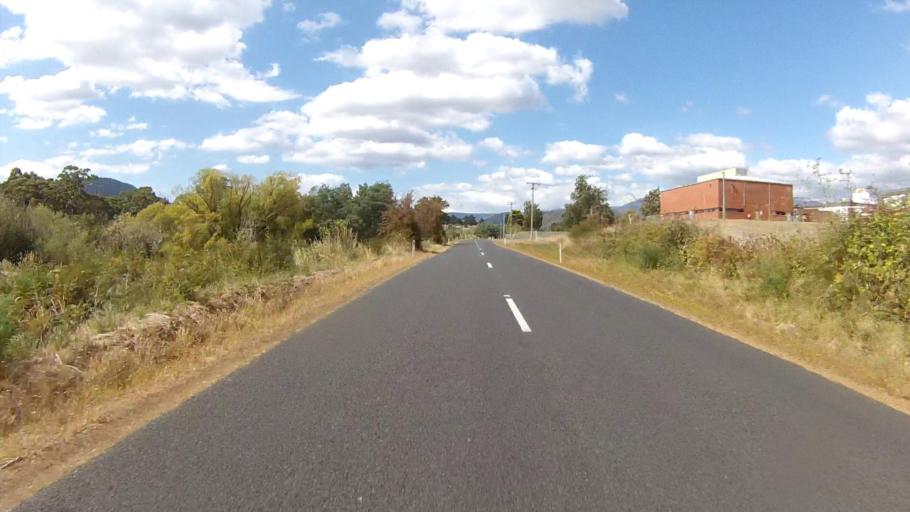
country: AU
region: Tasmania
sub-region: Derwent Valley
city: New Norfolk
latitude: -42.7663
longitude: 147.0192
